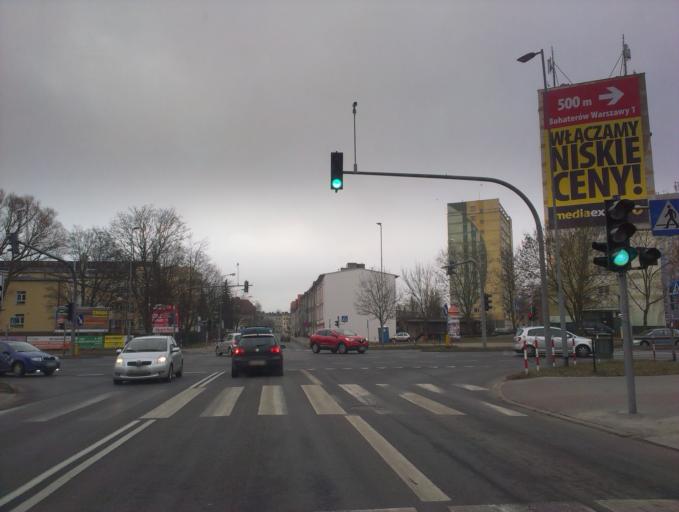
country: PL
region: West Pomeranian Voivodeship
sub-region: Koszalin
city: Koszalin
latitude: 54.1964
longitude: 16.1736
